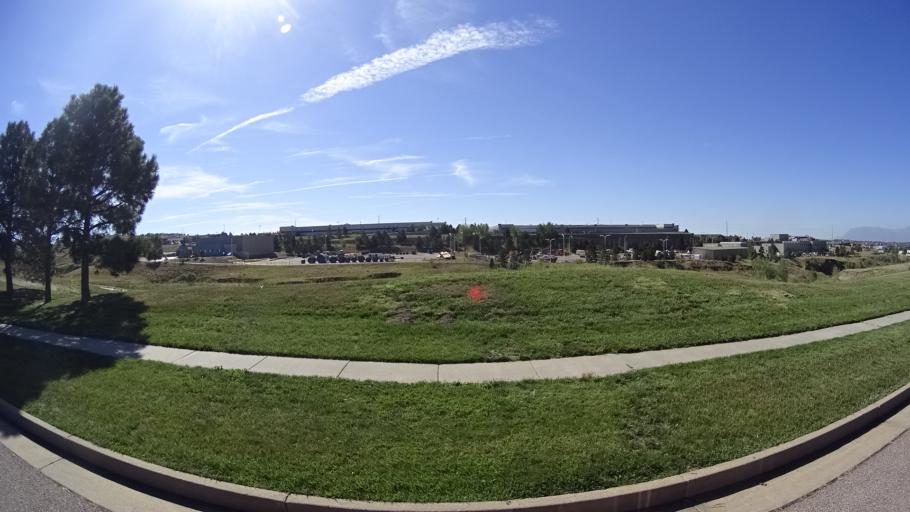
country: US
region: Colorado
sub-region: El Paso County
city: Black Forest
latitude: 38.9463
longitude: -104.7266
